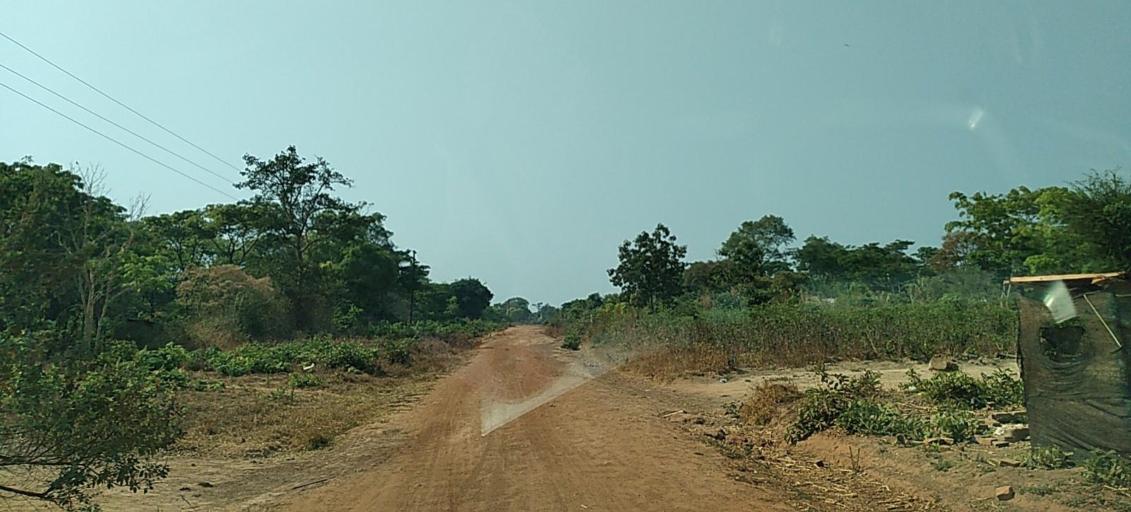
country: ZM
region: Copperbelt
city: Chingola
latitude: -12.9128
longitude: 27.3726
